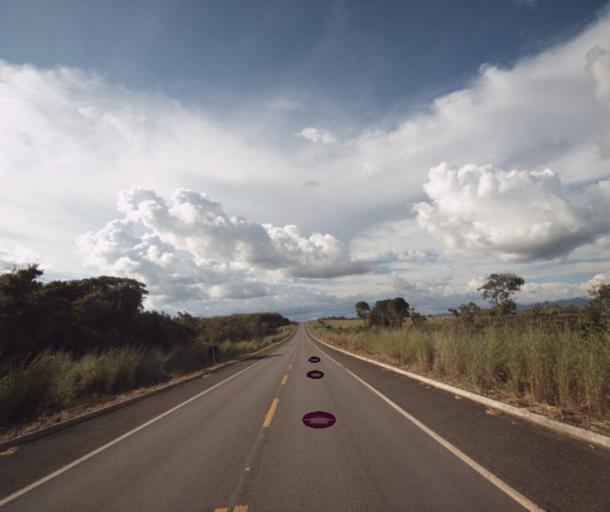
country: BR
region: Goias
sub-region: Barro Alto
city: Barro Alto
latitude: -14.8335
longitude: -48.6382
